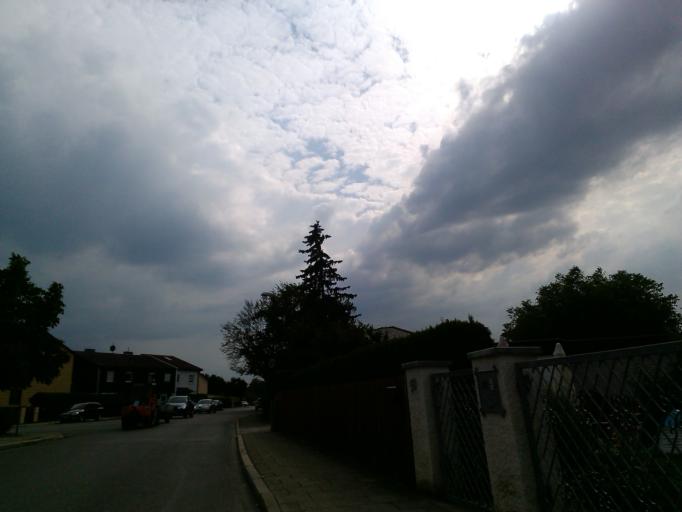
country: DE
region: Bavaria
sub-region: Upper Bavaria
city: Puchheim
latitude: 48.1328
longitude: 11.3526
